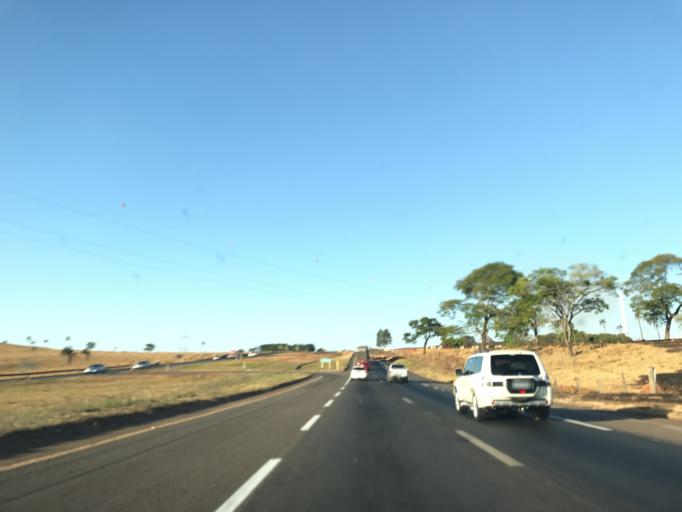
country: BR
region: Goias
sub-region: Goianapolis
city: Goianapolis
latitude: -16.4582
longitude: -49.0578
